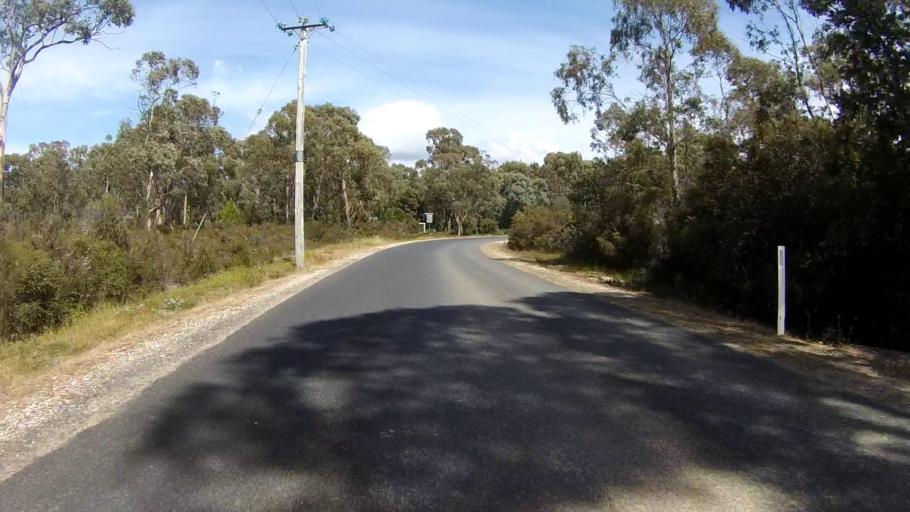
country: AU
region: Tasmania
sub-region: Huon Valley
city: Cygnet
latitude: -43.2456
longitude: 147.1062
